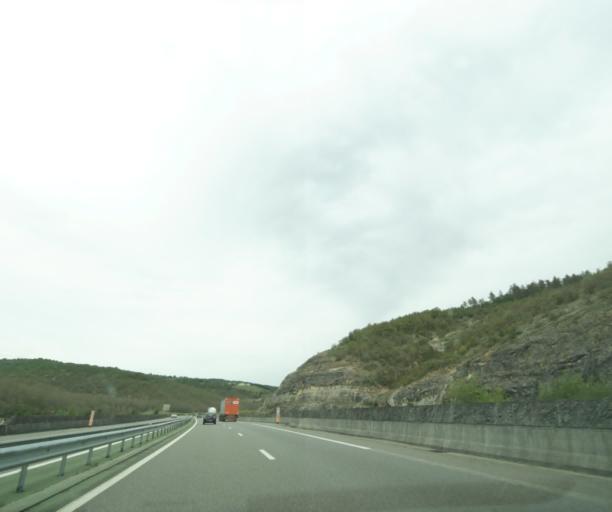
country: FR
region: Midi-Pyrenees
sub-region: Departement du Lot
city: Cahors
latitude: 44.4266
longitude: 1.5083
